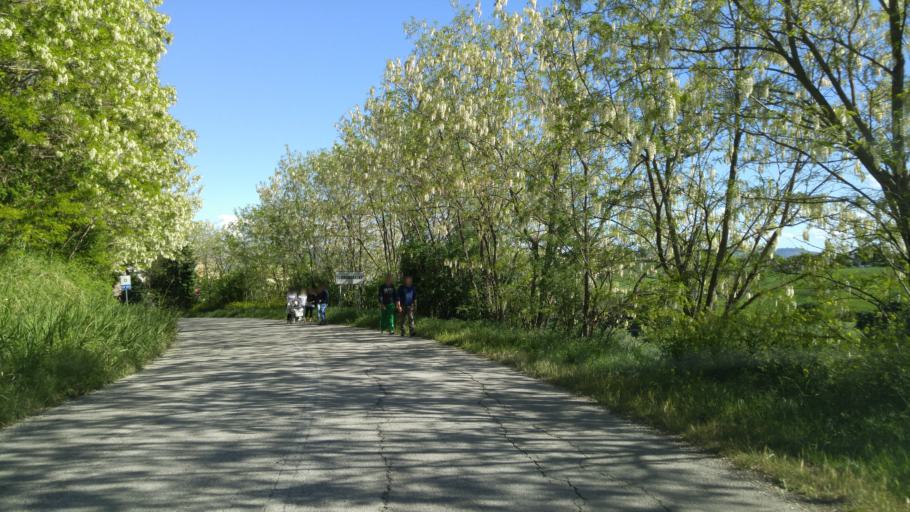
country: IT
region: The Marches
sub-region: Provincia di Pesaro e Urbino
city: Serrungarina
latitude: 43.7486
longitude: 12.8711
